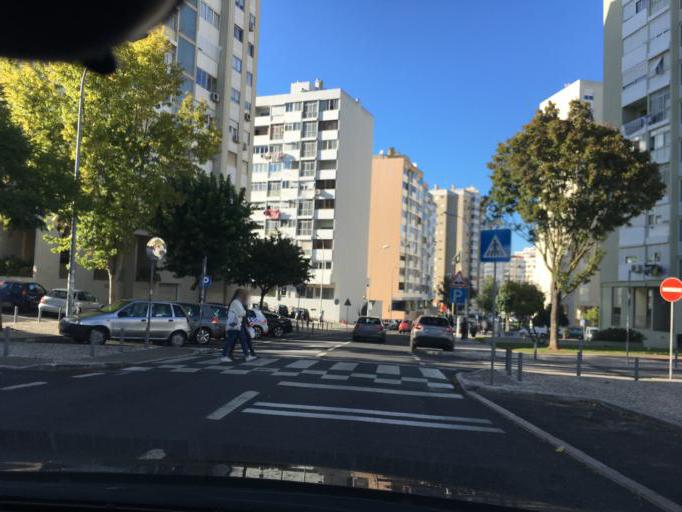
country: PT
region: Lisbon
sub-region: Odivelas
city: Pontinha
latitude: 38.7608
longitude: -9.2060
